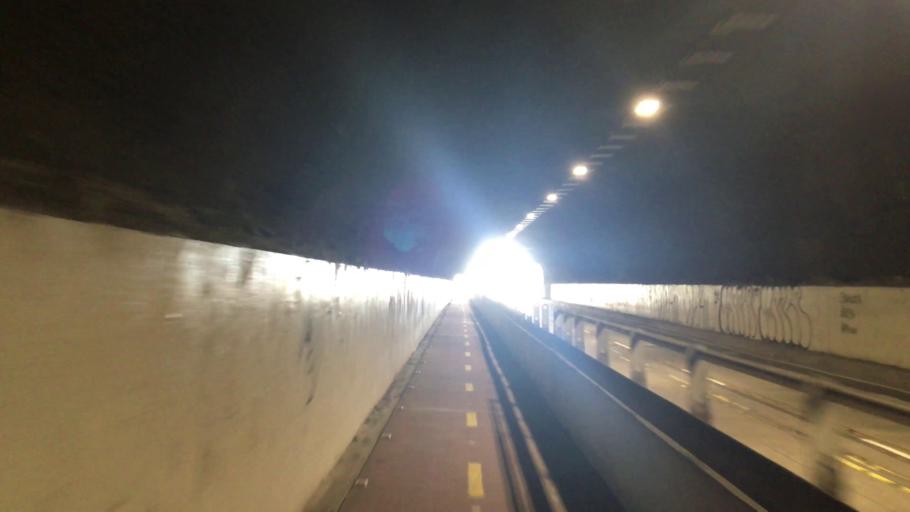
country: BR
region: Rio de Janeiro
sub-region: Rio De Janeiro
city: Rio de Janeiro
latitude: -23.0112
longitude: -43.2901
